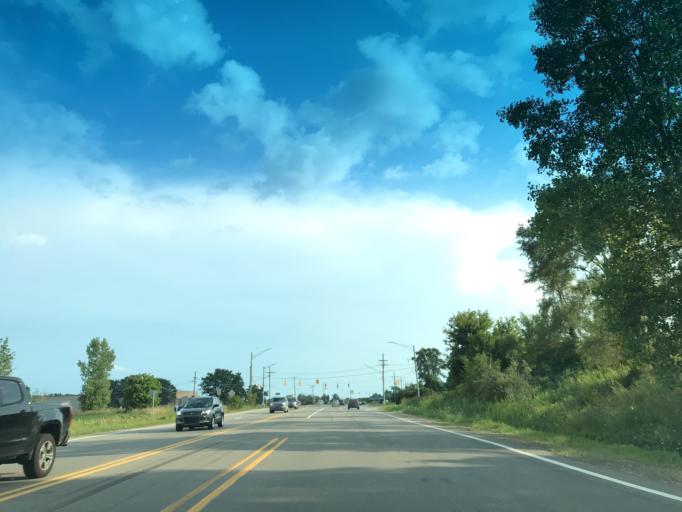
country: US
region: Michigan
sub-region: Oakland County
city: Milford
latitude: 42.5241
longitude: -83.6160
